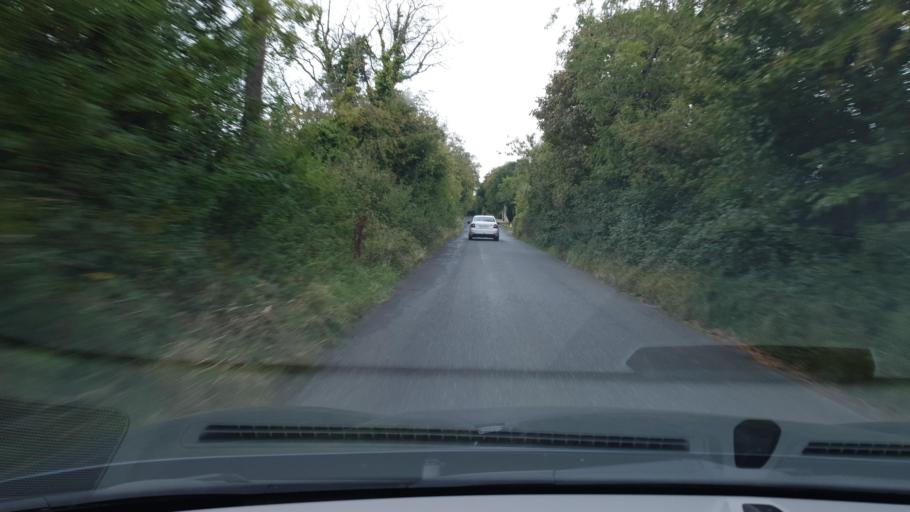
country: IE
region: Leinster
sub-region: An Mhi
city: Dunshaughlin
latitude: 53.5290
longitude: -6.5396
